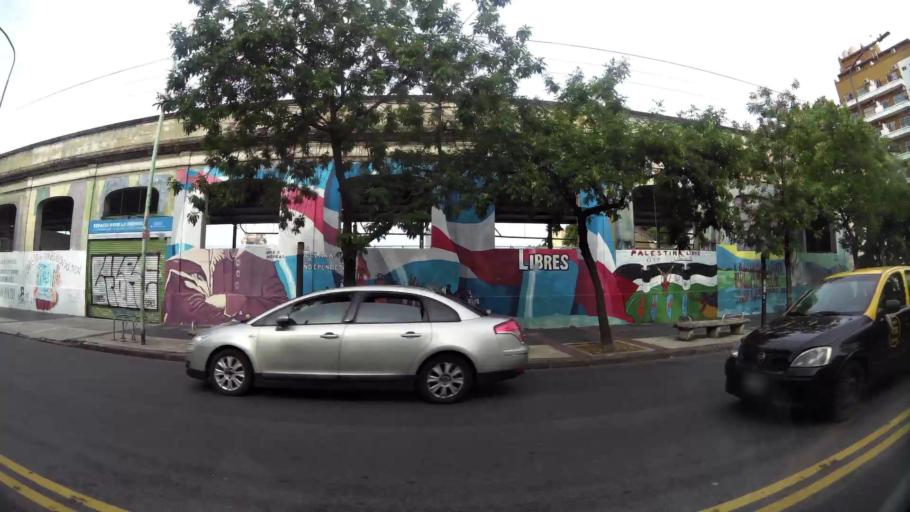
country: AR
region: Buenos Aires F.D.
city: Villa Santa Rita
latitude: -34.6375
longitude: -58.4869
